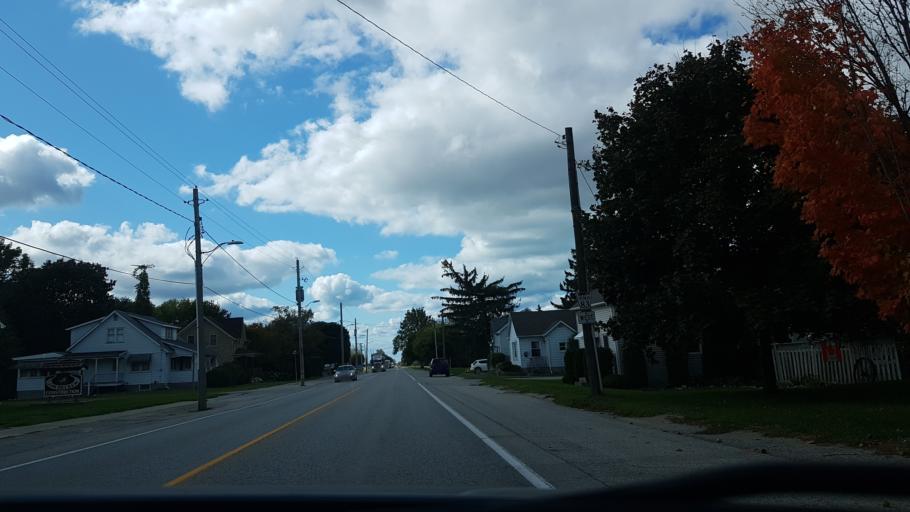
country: CA
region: Ontario
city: South Huron
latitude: 43.3459
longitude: -81.6376
